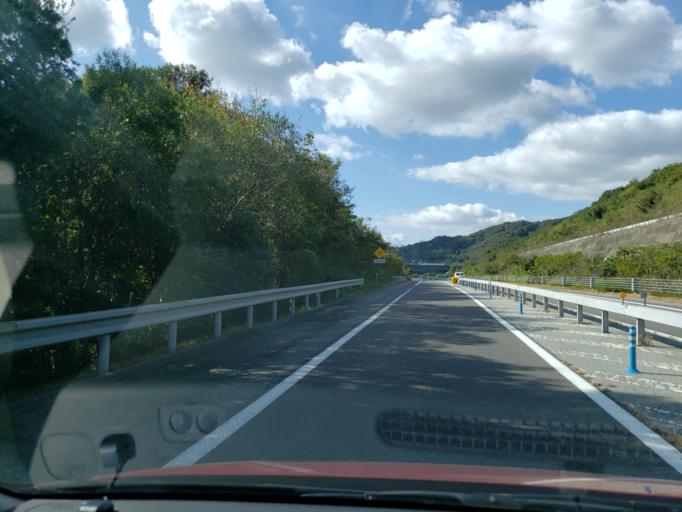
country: JP
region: Tokushima
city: Ishii
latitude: 34.1376
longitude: 134.4003
